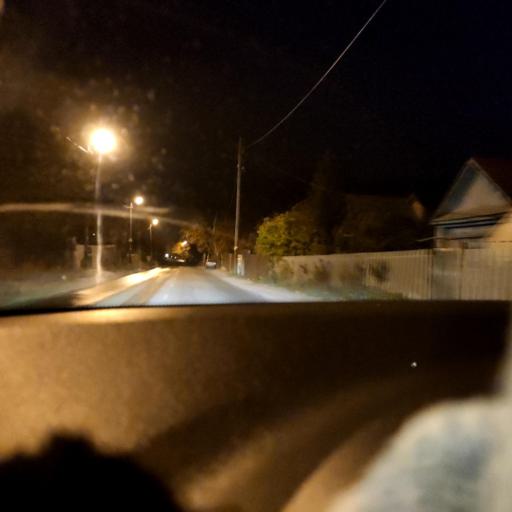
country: RU
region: Samara
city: Samara
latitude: 53.2406
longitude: 50.2601
